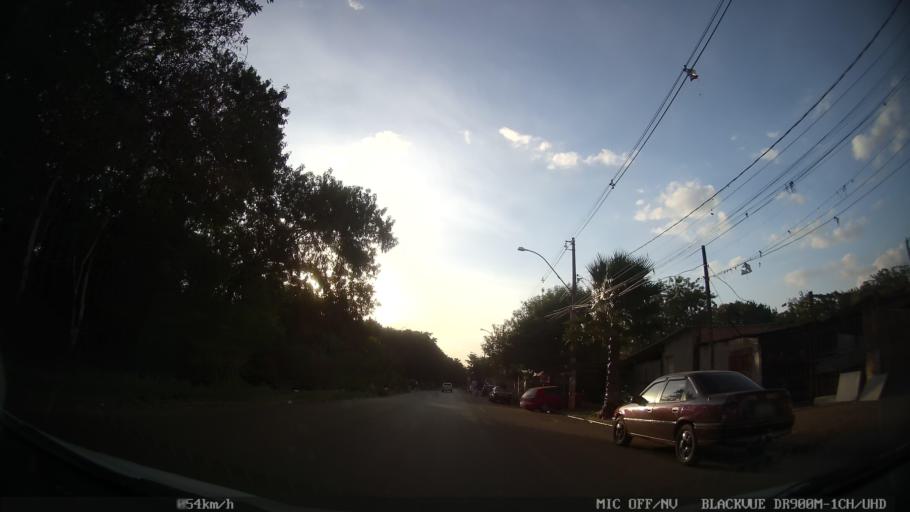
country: BR
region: Sao Paulo
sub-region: Ribeirao Preto
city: Ribeirao Preto
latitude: -21.1139
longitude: -47.8054
